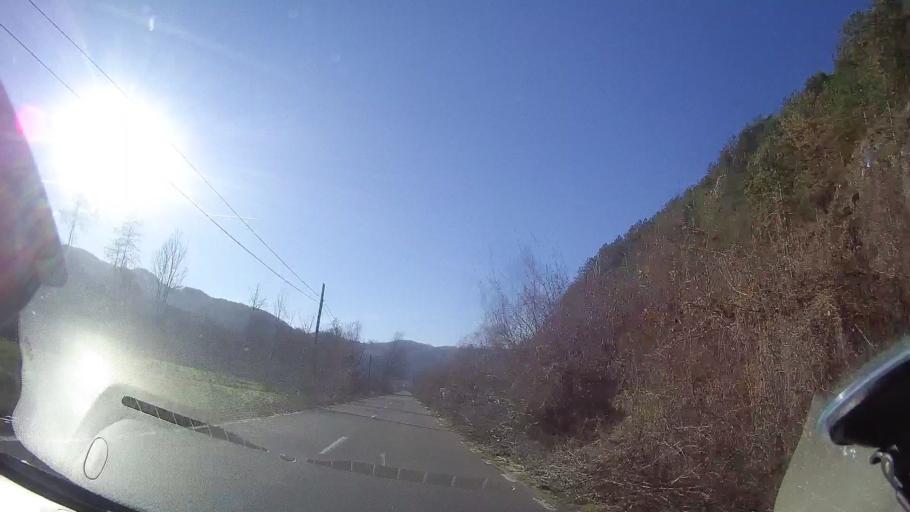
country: RO
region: Bihor
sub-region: Comuna Bratca
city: Bratca
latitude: 46.9260
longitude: 22.6296
